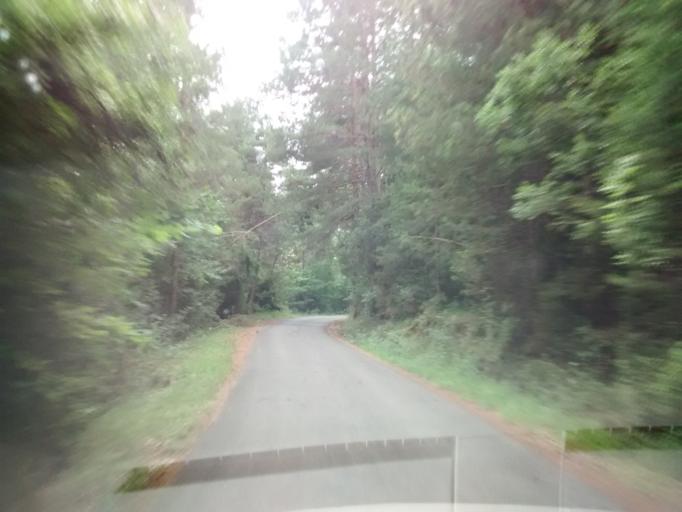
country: ES
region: Aragon
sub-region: Provincia de Huesca
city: Puertolas
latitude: 42.5807
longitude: 0.1424
